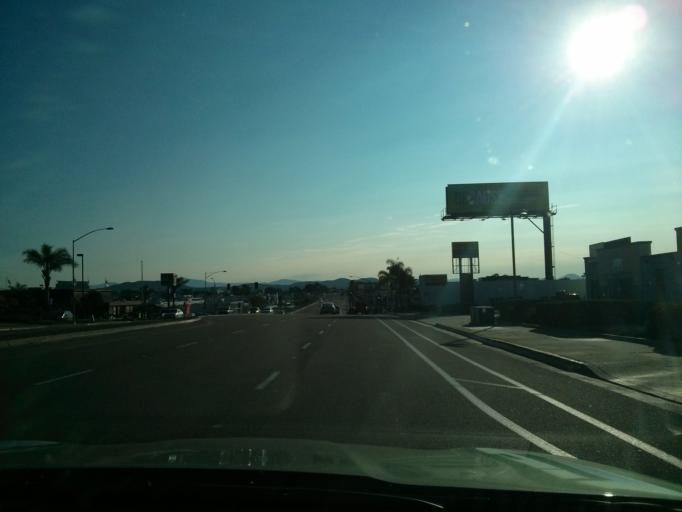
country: US
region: California
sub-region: San Diego County
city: San Diego
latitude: 32.8216
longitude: -117.1567
